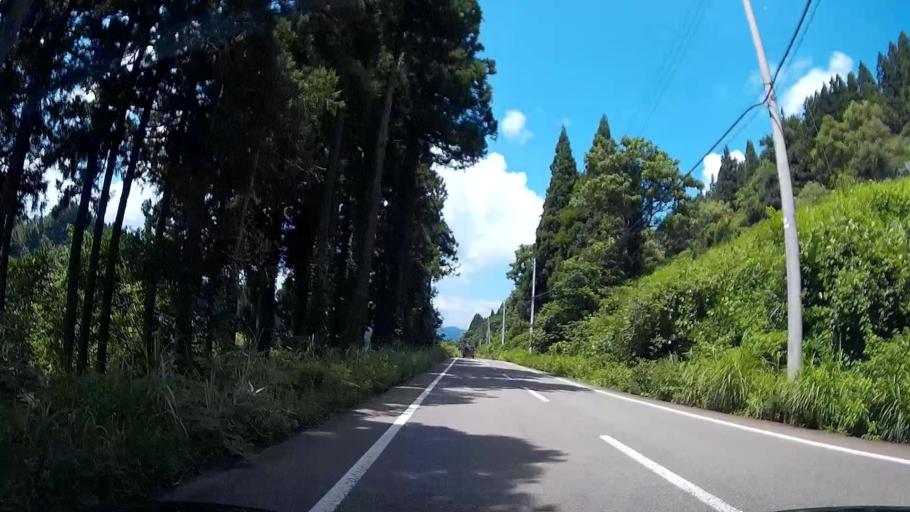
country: JP
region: Niigata
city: Tokamachi
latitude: 37.0795
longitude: 138.7540
